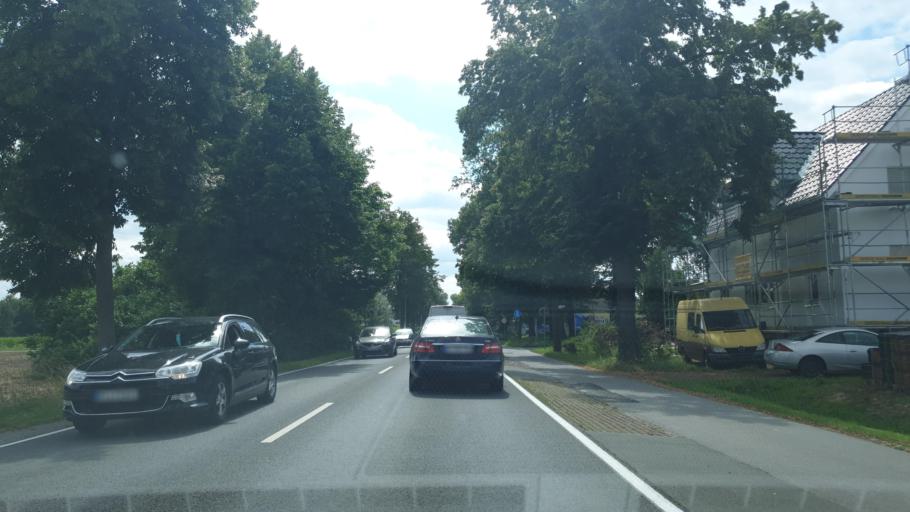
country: DE
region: North Rhine-Westphalia
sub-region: Regierungsbezirk Detmold
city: Steinhagen
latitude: 51.9750
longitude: 8.4707
